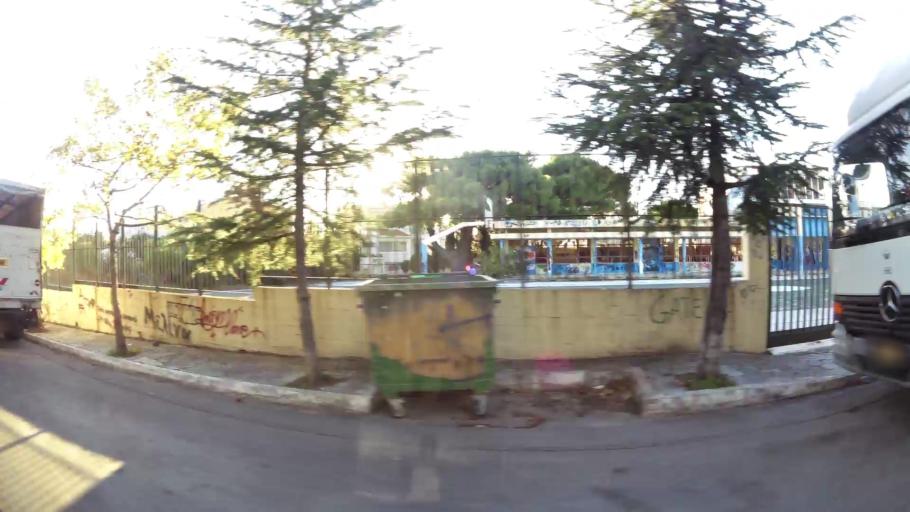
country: GR
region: Attica
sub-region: Nomarchia Anatolikis Attikis
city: Kryoneri
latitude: 38.1378
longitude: 23.8327
